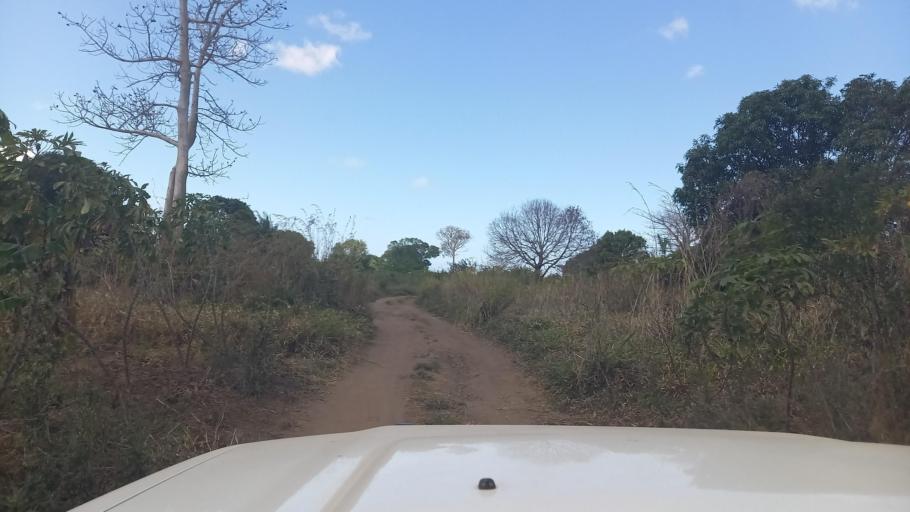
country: MZ
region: Cabo Delgado
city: Pemba
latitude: -13.4248
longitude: 40.4950
